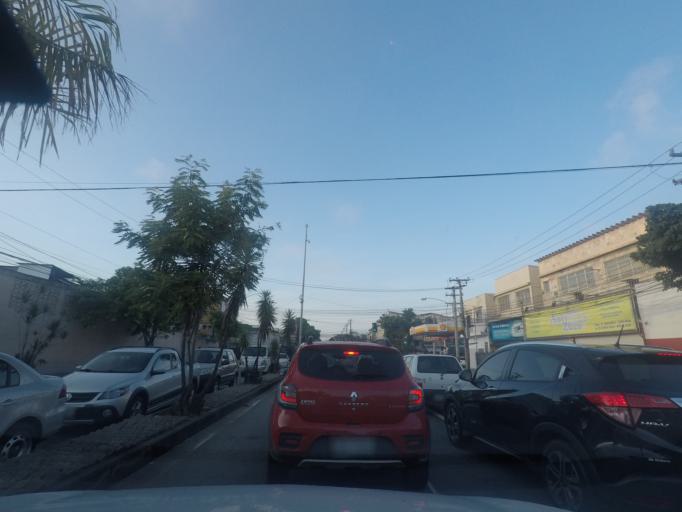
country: BR
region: Rio de Janeiro
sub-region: Duque De Caxias
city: Duque de Caxias
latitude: -22.8288
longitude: -43.2766
